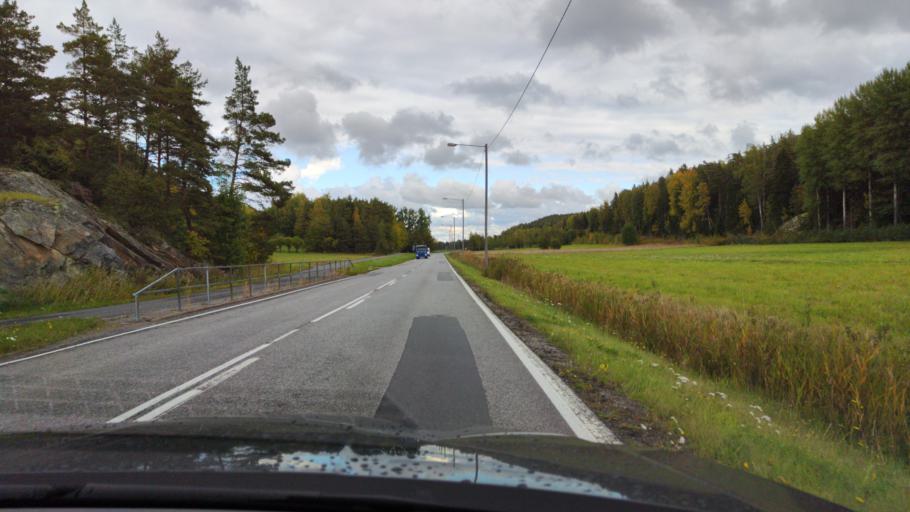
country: FI
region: Varsinais-Suomi
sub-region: Turku
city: Raisio
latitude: 60.3594
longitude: 22.1795
